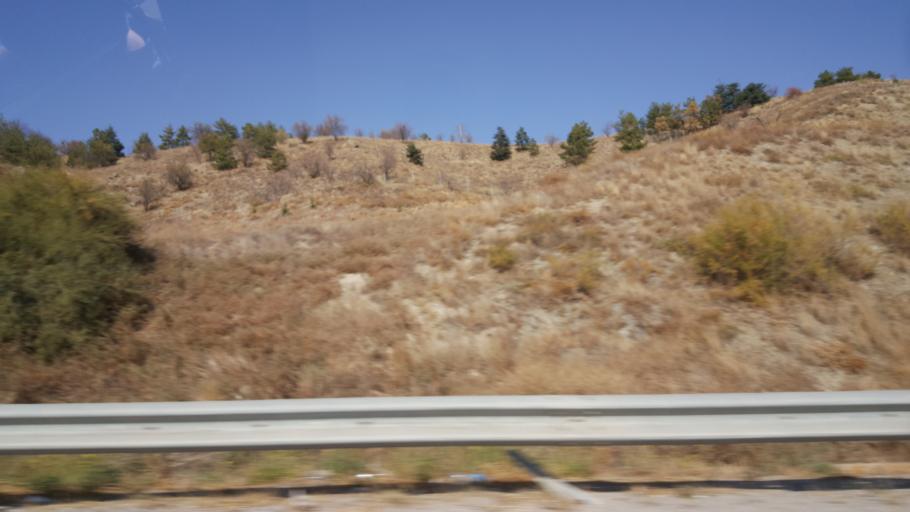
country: TR
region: Ankara
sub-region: Goelbasi
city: Golbasi
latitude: 39.8143
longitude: 32.8144
